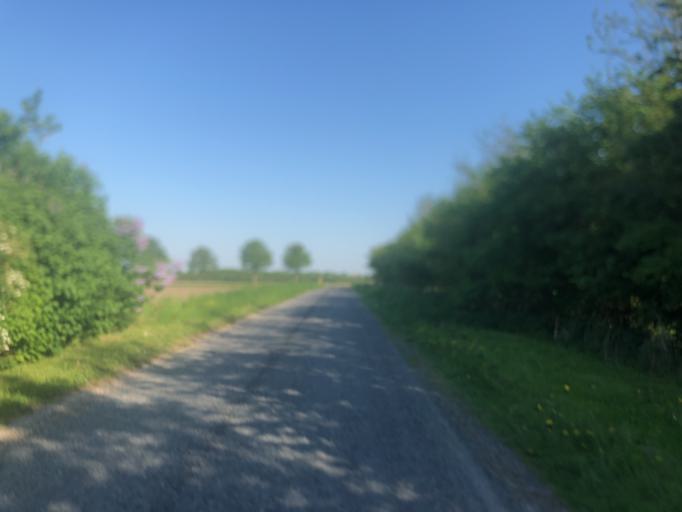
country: DK
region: Zealand
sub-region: Ringsted Kommune
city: Ringsted
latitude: 55.4726
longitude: 11.8216
